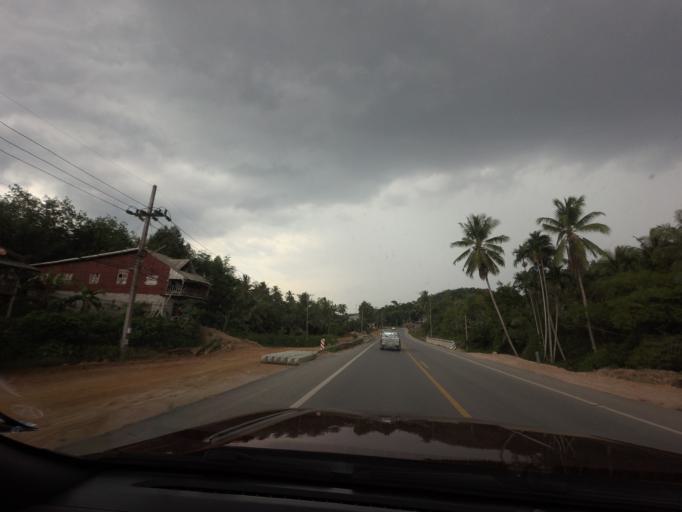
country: TH
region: Yala
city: Krong Pi Nang
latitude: 6.4038
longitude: 101.2816
